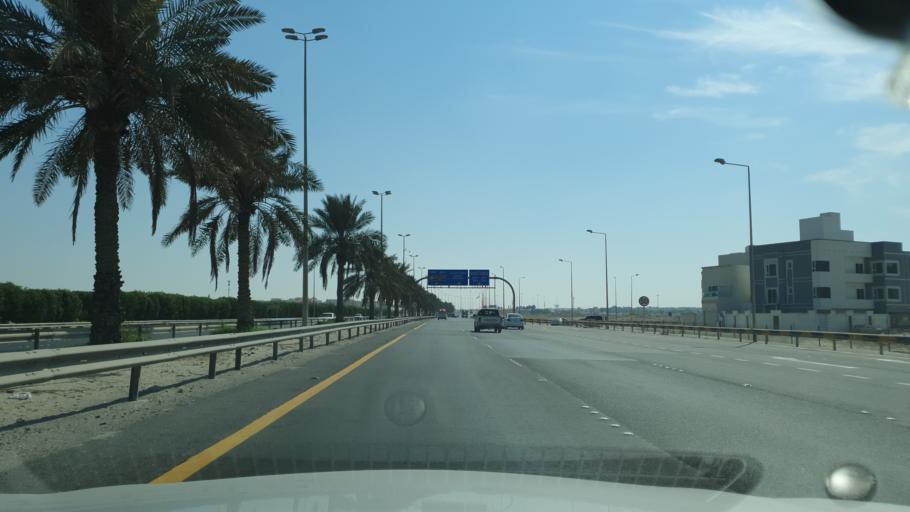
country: BH
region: Central Governorate
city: Madinat Hamad
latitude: 26.1504
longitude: 50.5078
